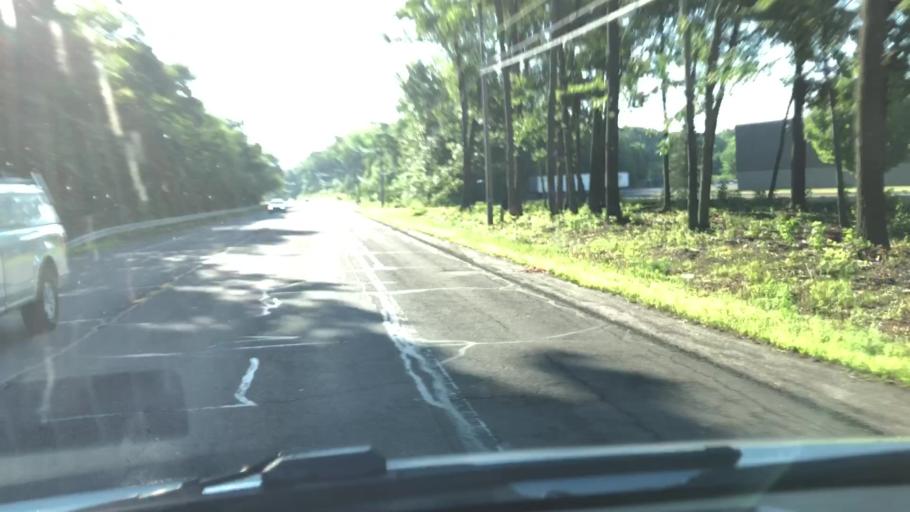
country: US
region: Massachusetts
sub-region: Franklin County
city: South Deerfield
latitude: 42.4677
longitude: -72.6047
